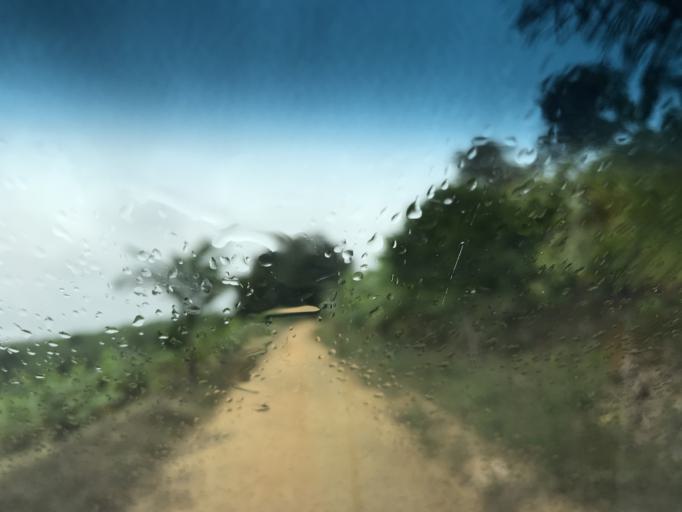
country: BR
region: Bahia
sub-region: Ibirapitanga
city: Ibirapitanga
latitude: -14.0477
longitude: -39.3582
